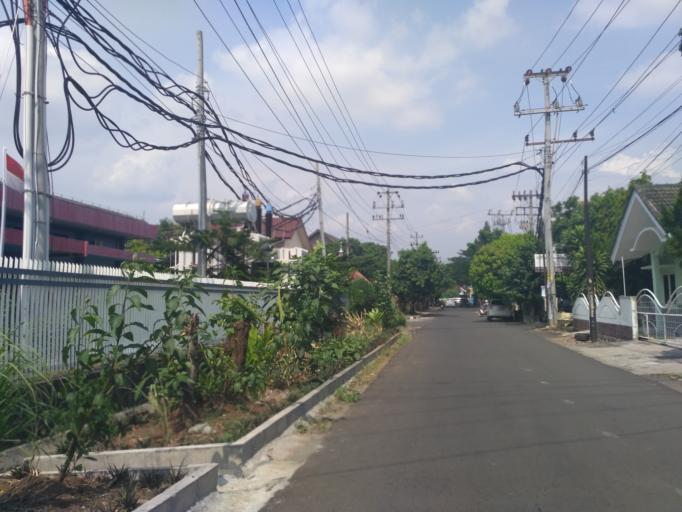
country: ID
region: Central Java
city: Semarang
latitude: -7.0503
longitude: 110.4264
